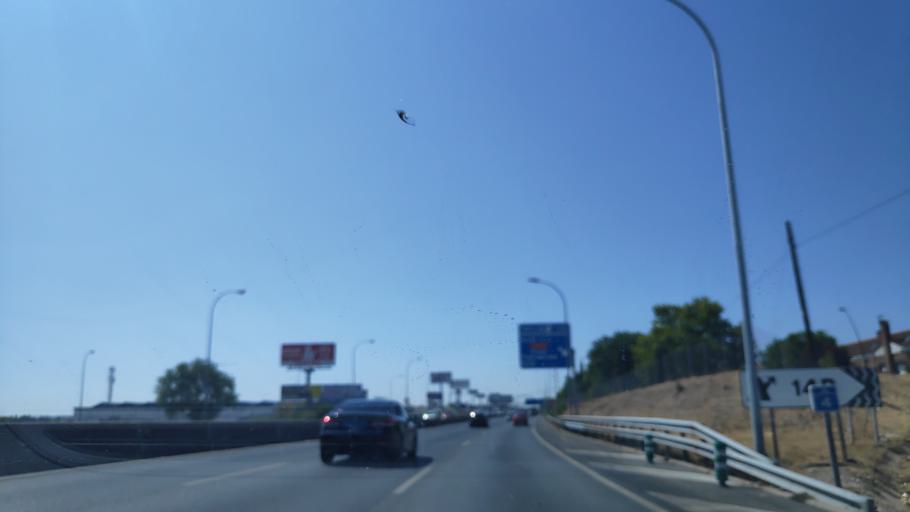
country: ES
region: Madrid
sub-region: Provincia de Madrid
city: Getafe
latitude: 40.2952
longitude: -3.7380
